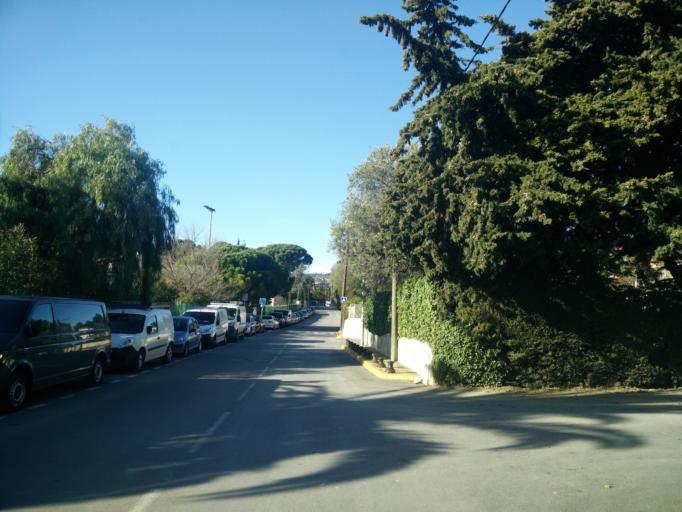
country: FR
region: Provence-Alpes-Cote d'Azur
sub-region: Departement des Bouches-du-Rhone
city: Cassis
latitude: 43.2119
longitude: 5.5445
